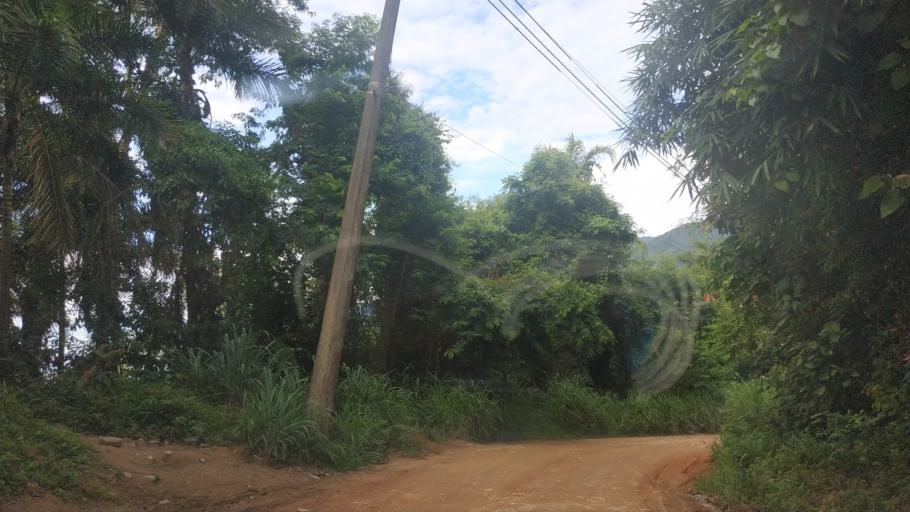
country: BR
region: Sao Paulo
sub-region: Ilhabela
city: Ilhabela
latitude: -23.8337
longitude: -45.3583
